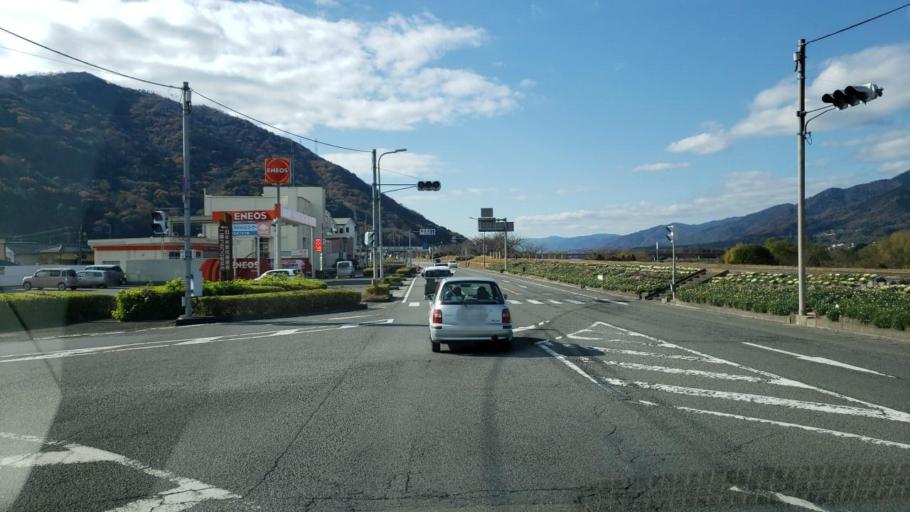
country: JP
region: Tokushima
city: Wakimachi
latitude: 34.0437
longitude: 134.0637
